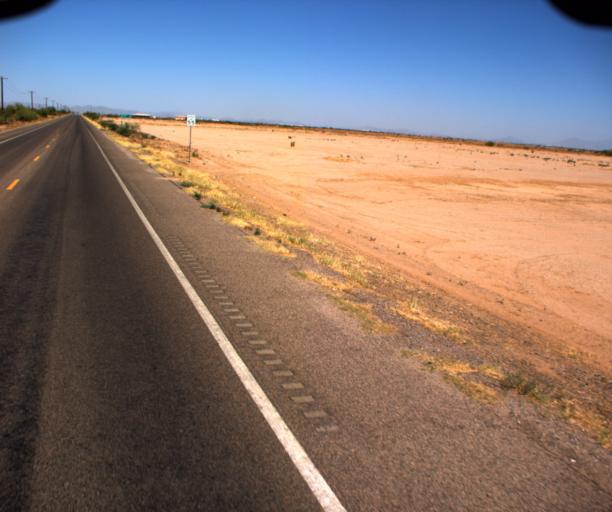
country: US
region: Arizona
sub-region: Pinal County
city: Casa Grande
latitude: 32.8795
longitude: -111.8641
